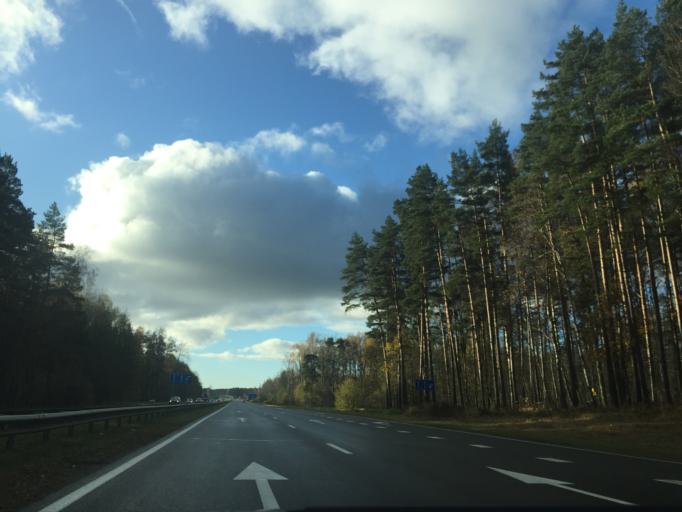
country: LV
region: Babite
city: Pinki
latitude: 56.9367
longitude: 23.9187
